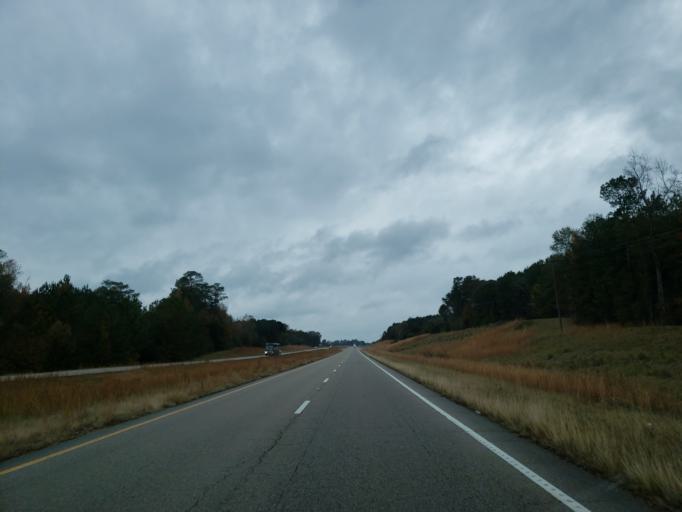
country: US
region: Mississippi
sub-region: Wayne County
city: Waynesboro
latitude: 31.7511
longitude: -88.6580
